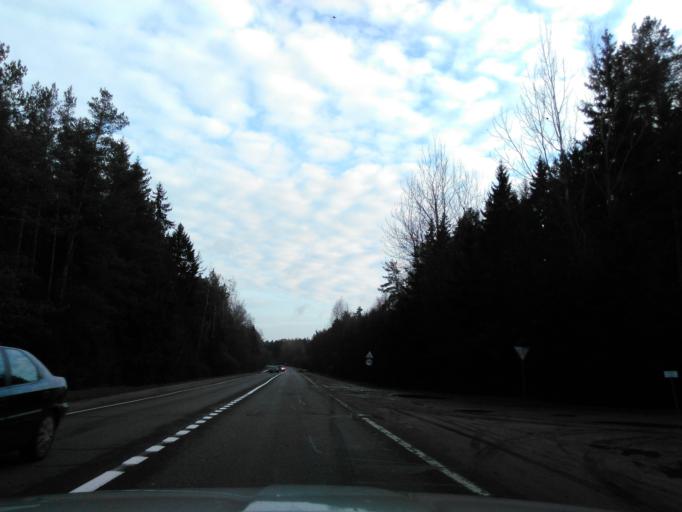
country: BY
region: Minsk
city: Plyeshchanitsy
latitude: 54.3872
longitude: 27.8724
